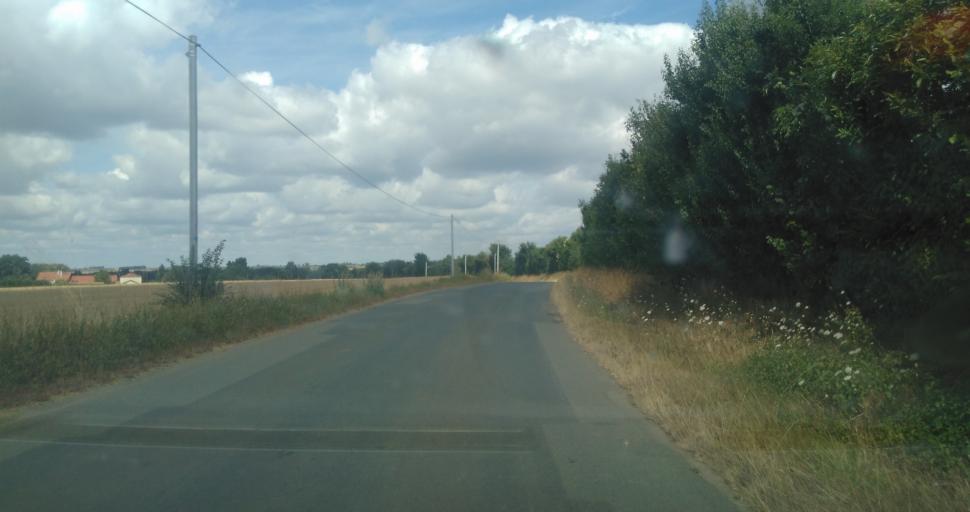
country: FR
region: Pays de la Loire
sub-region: Departement de la Vendee
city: Sainte-Hermine
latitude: 46.5303
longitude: -1.0812
